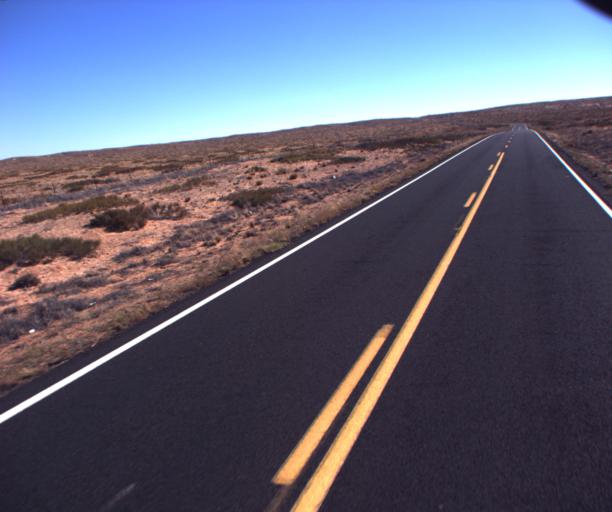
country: US
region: Arizona
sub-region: Coconino County
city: Tuba City
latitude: 36.0226
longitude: -111.1366
